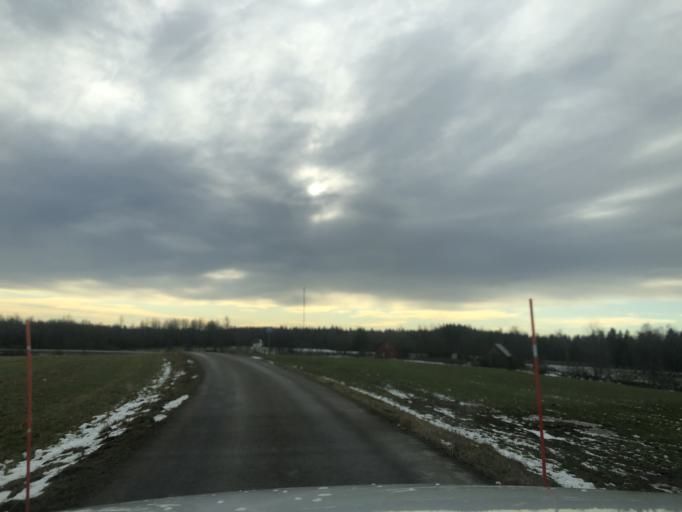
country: SE
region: Vaestra Goetaland
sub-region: Ulricehamns Kommun
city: Ulricehamn
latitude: 57.8040
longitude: 13.5069
